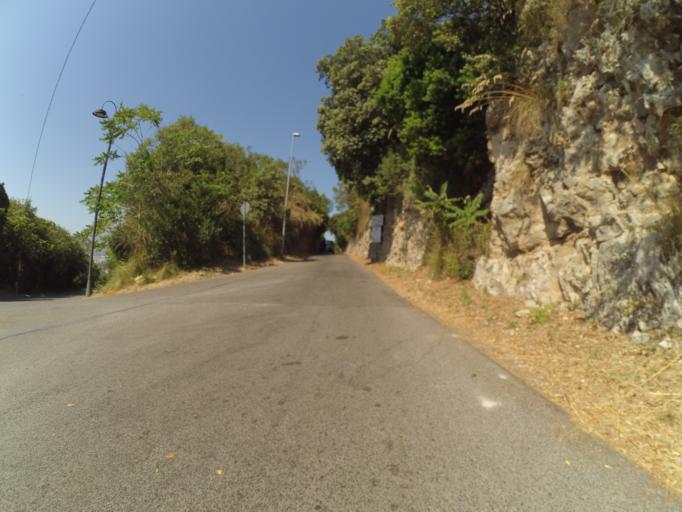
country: IT
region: Latium
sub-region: Provincia di Latina
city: Gaeta
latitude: 41.2093
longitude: 13.5730
